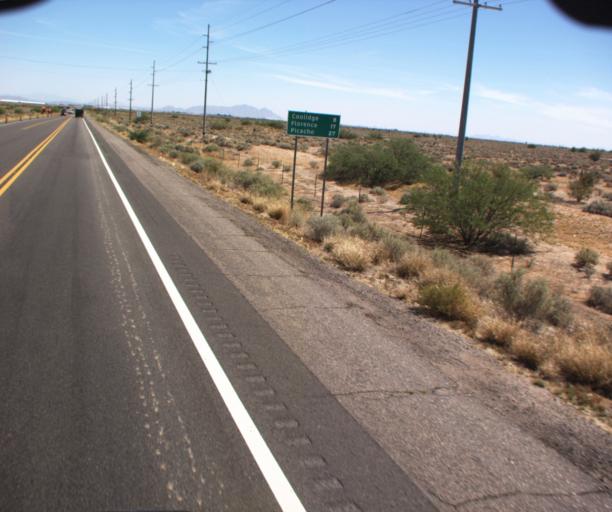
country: US
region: Arizona
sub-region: Pinal County
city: Blackwater
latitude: 33.0209
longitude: -111.6353
